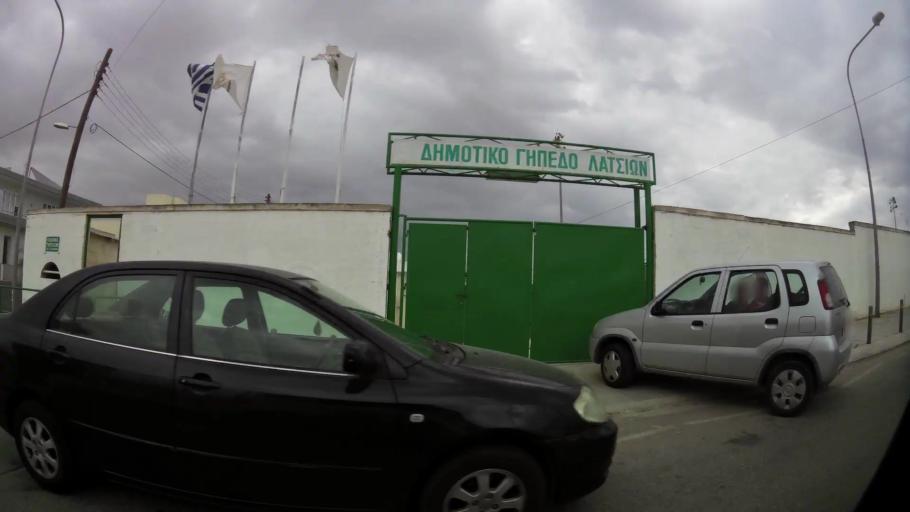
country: CY
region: Lefkosia
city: Geri
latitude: 35.1141
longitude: 33.3905
